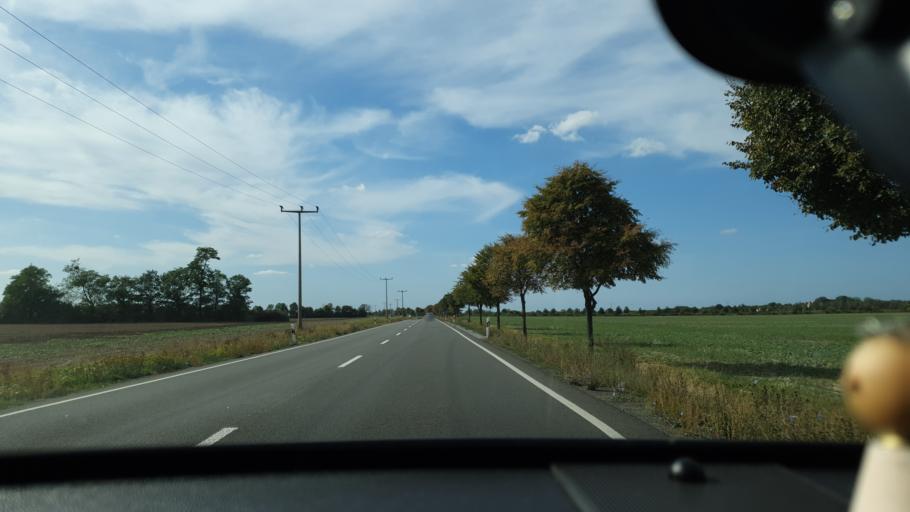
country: DE
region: Saxony
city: Jesewitz
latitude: 51.4573
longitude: 12.5415
